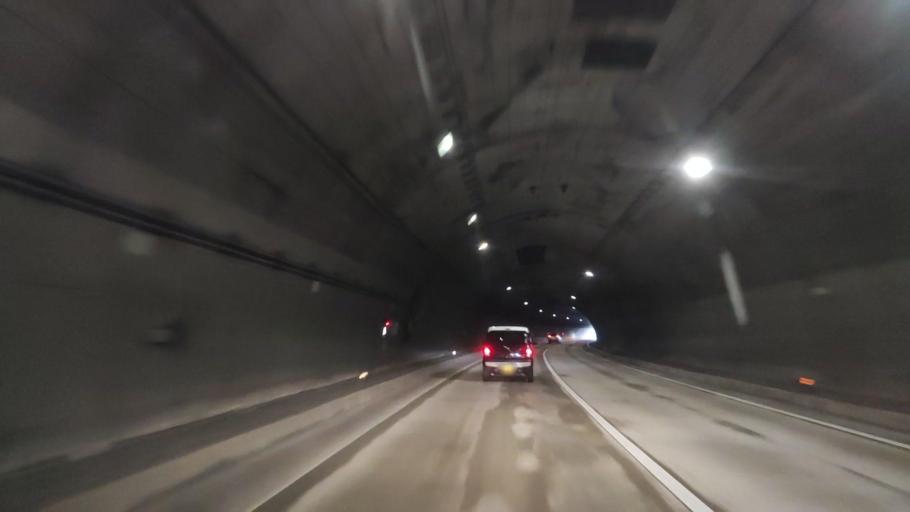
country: JP
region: Hiroshima
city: Onomichi
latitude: 34.4464
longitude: 133.2287
